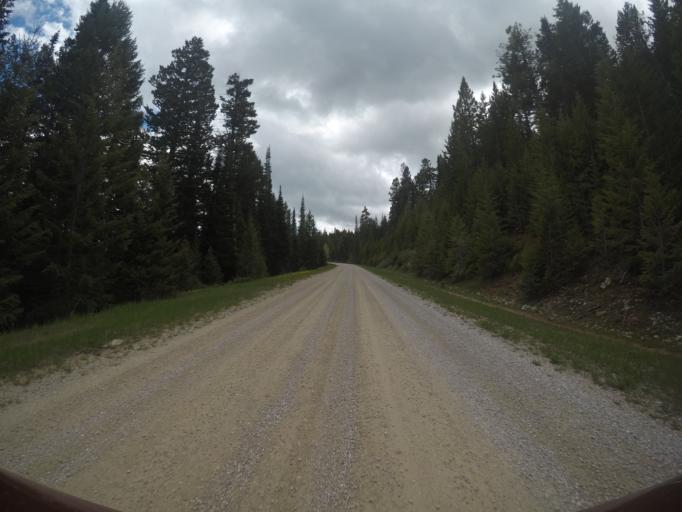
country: US
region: Wyoming
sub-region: Big Horn County
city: Lovell
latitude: 45.1806
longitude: -108.4663
